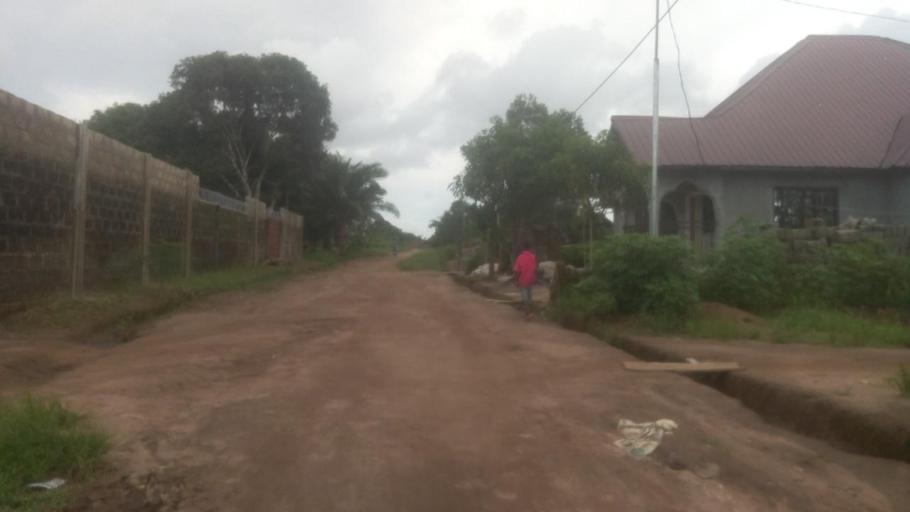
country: SL
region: Northern Province
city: Masoyila
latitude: 8.6053
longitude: -13.1901
